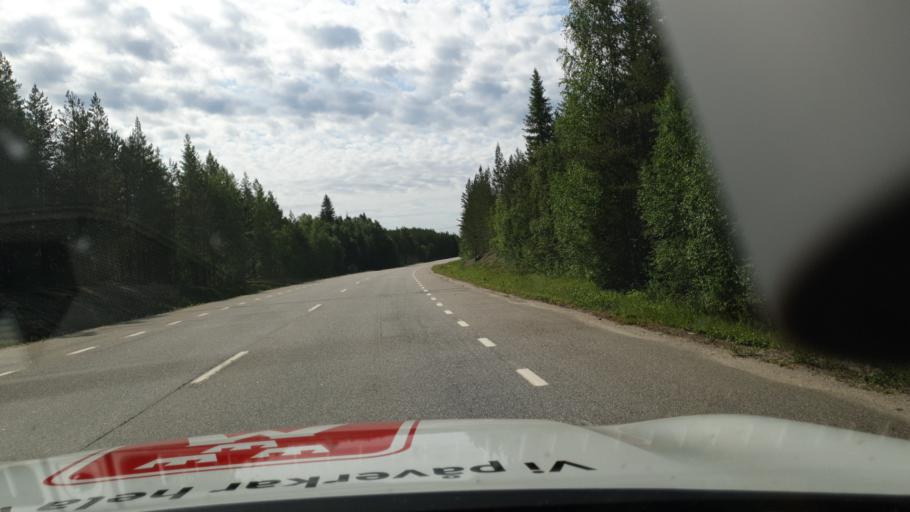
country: SE
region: Vaesterbotten
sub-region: Norsjo Kommun
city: Norsjoe
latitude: 64.5957
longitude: 19.2988
